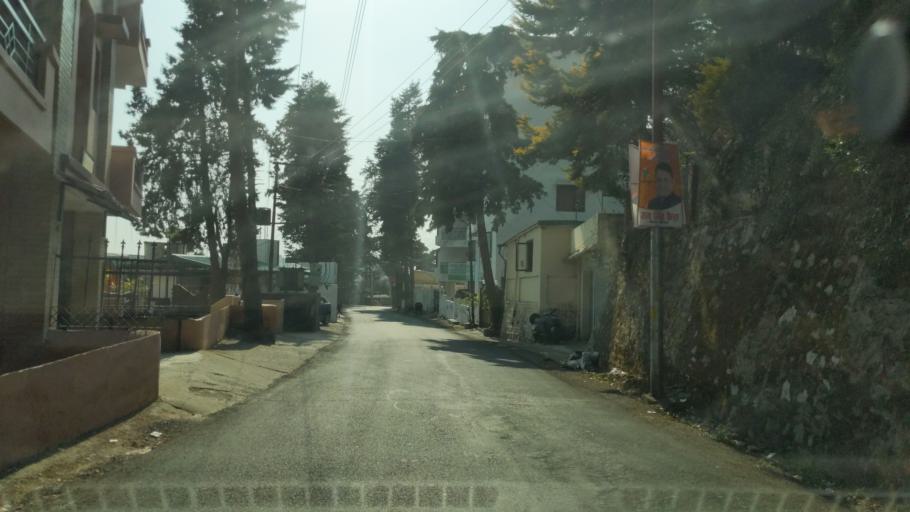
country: IN
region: Uttarakhand
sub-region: Naini Tal
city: Bhowali
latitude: 29.3888
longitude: 79.5306
